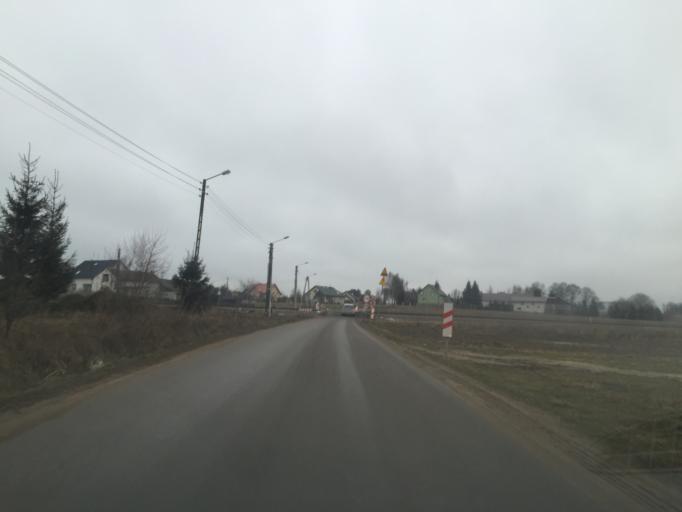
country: PL
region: Pomeranian Voivodeship
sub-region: Powiat kartuski
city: Banino
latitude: 54.3911
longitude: 18.4295
